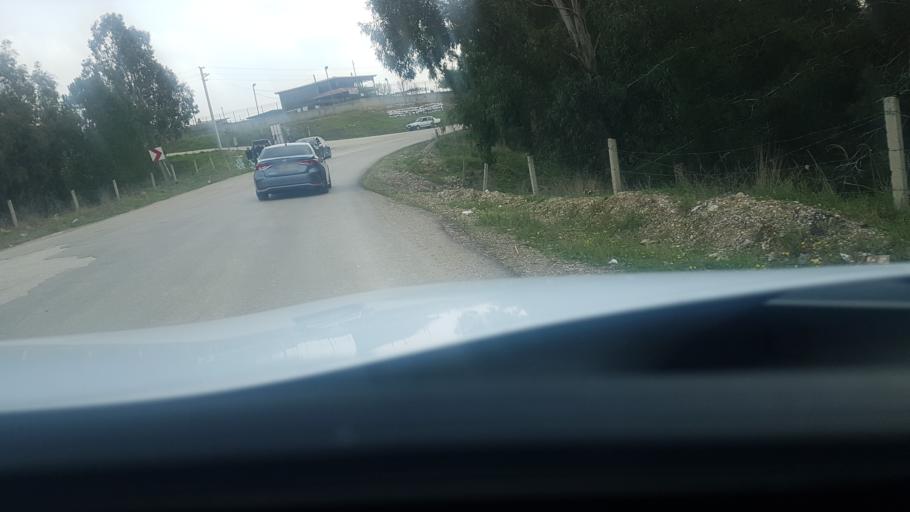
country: TR
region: Adana
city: Seyhan
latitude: 37.0604
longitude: 35.2572
